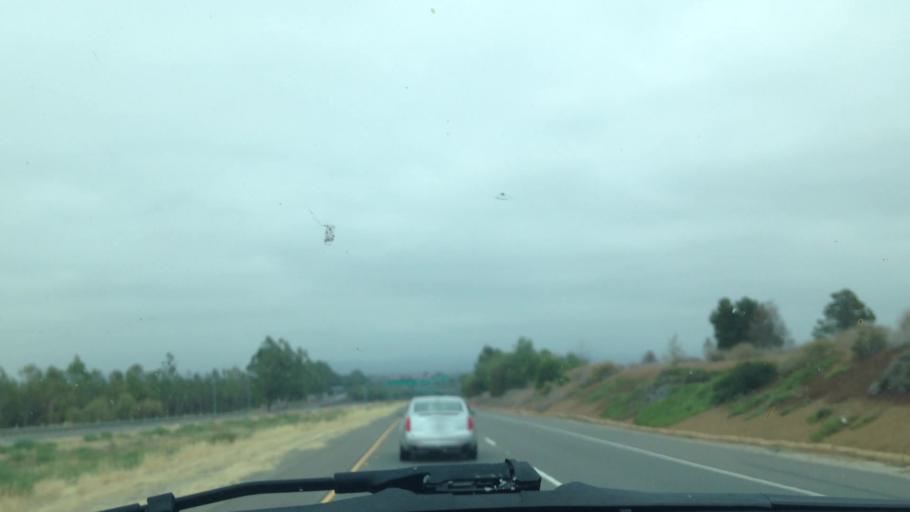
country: US
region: California
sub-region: Orange County
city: North Tustin
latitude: 33.7494
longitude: -117.7649
